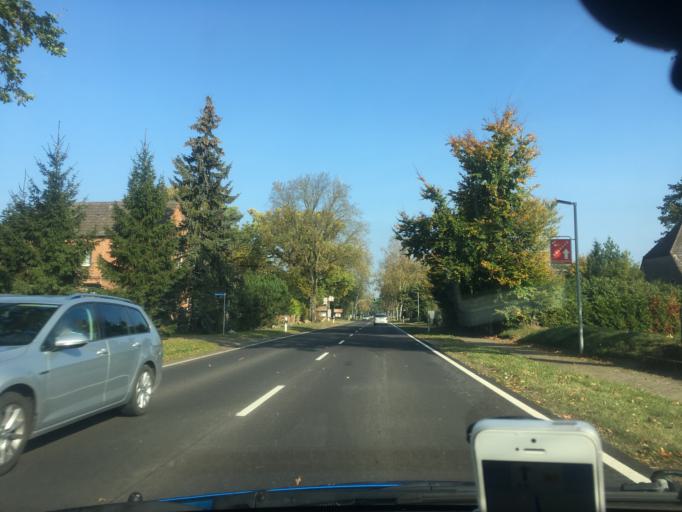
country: DE
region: Mecklenburg-Vorpommern
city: Stralendorf
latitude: 53.4948
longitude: 11.2846
